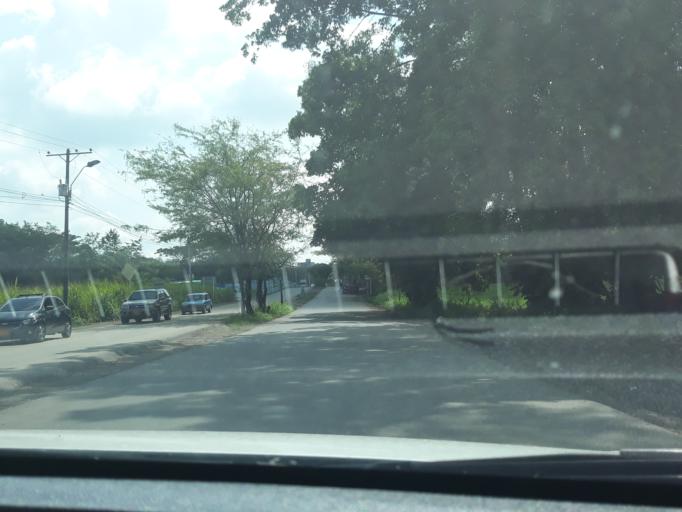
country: CO
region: Valle del Cauca
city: Cali
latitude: 3.3590
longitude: -76.5236
